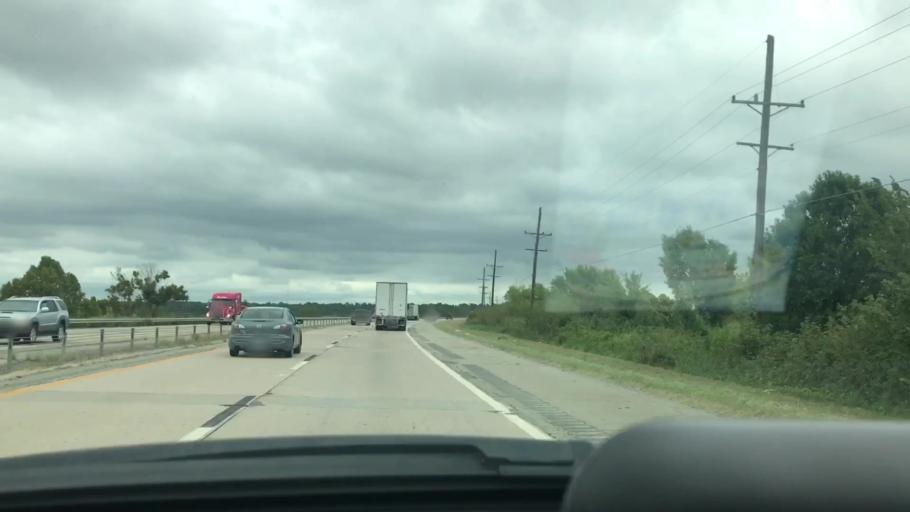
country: US
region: Oklahoma
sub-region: McIntosh County
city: Eufaula
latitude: 35.3400
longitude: -95.5852
